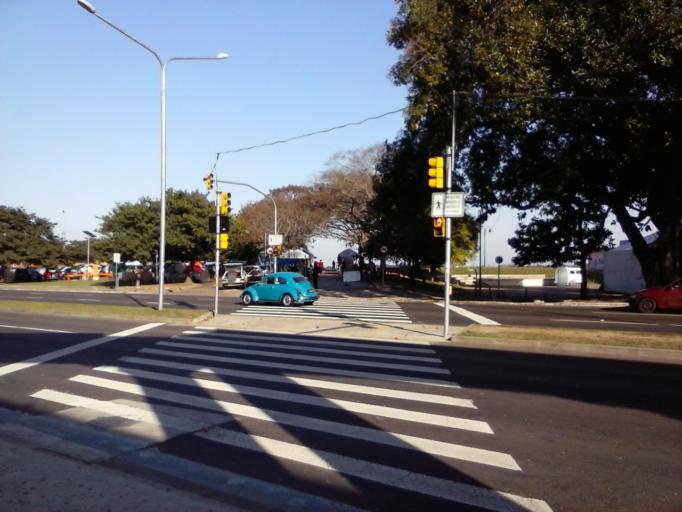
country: BR
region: Rio Grande do Sul
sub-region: Porto Alegre
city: Porto Alegre
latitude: -30.0346
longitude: -51.2403
